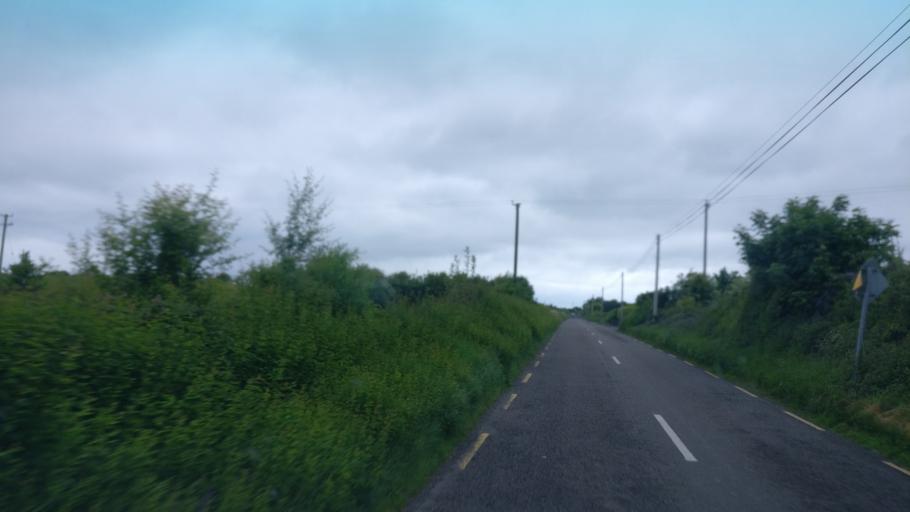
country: IE
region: Connaught
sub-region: County Galway
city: Portumna
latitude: 53.1088
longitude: -8.2680
